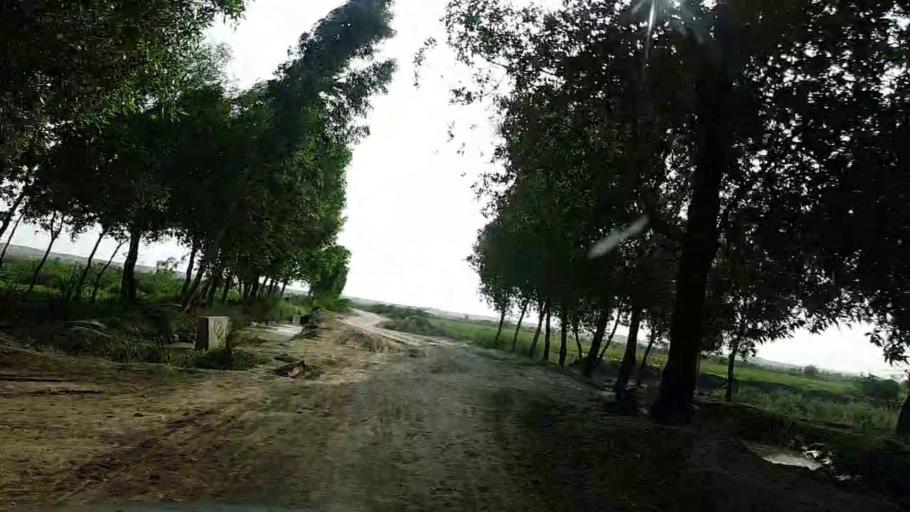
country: PK
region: Sindh
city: Kotri
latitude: 25.1863
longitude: 68.2577
